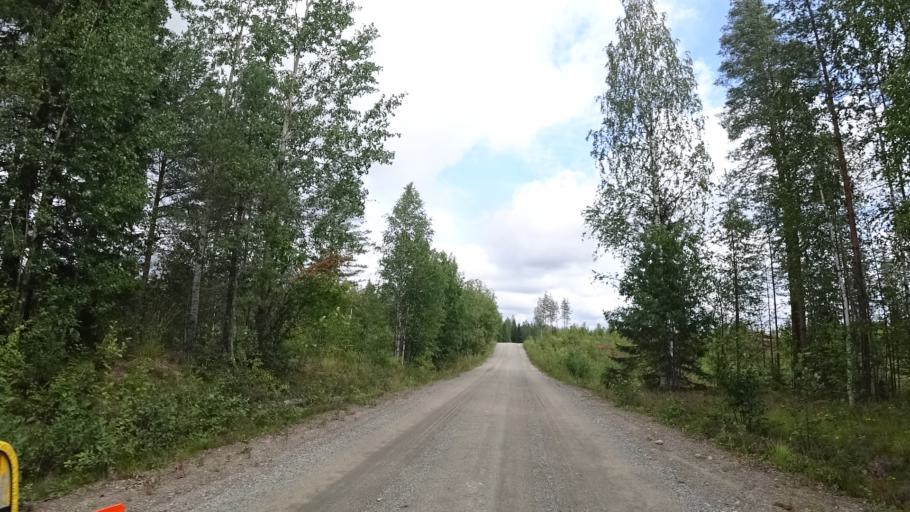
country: FI
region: North Karelia
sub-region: Joensuu
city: Ilomantsi
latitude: 62.9249
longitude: 31.3592
